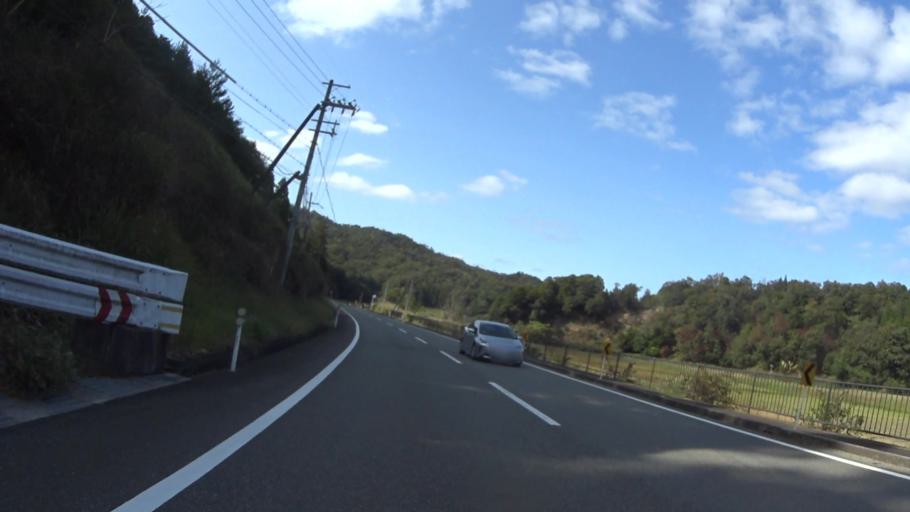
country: JP
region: Hyogo
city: Toyooka
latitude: 35.5645
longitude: 134.9775
